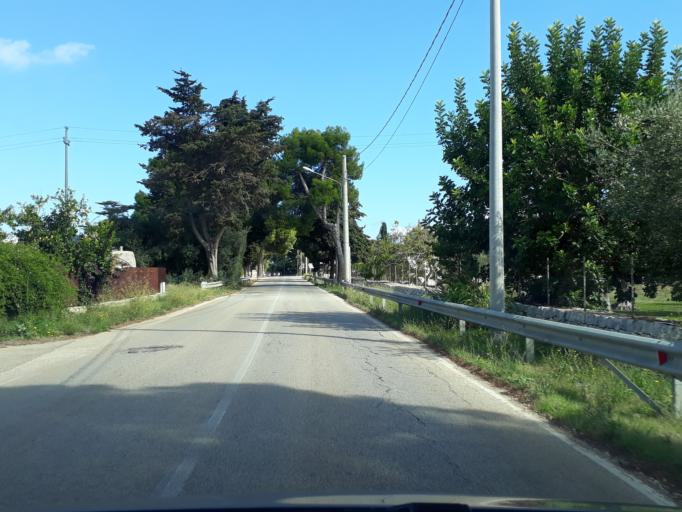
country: IT
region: Apulia
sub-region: Provincia di Bari
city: Mola di Bari
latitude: 41.0339
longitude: 17.0464
